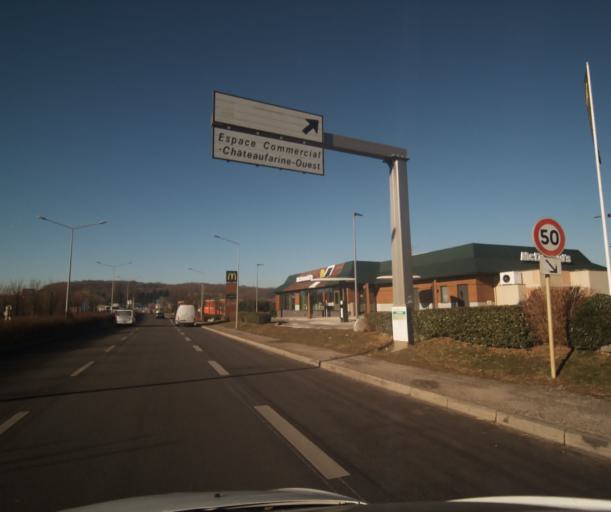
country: FR
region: Franche-Comte
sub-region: Departement du Doubs
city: Franois
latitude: 47.2209
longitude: 5.9502
